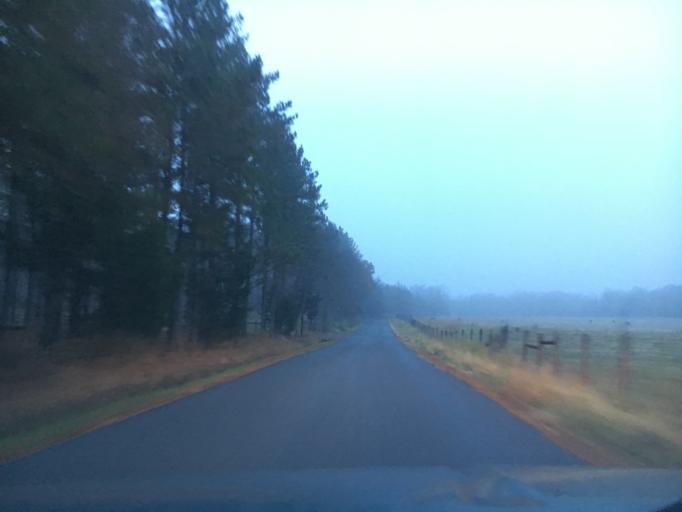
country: US
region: Virginia
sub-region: Halifax County
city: Mountain Road
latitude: 36.6841
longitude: -79.0323
